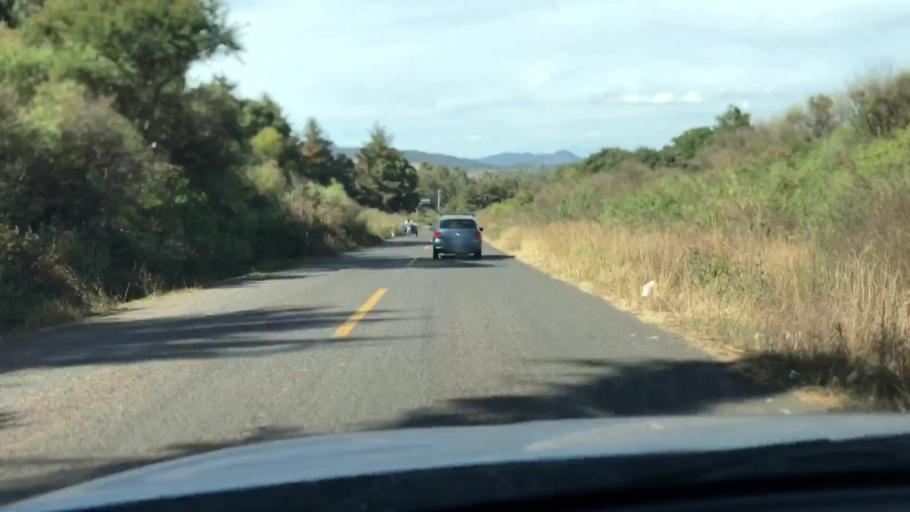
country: MX
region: Jalisco
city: Chiquilistlan
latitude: 20.1461
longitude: -103.7244
